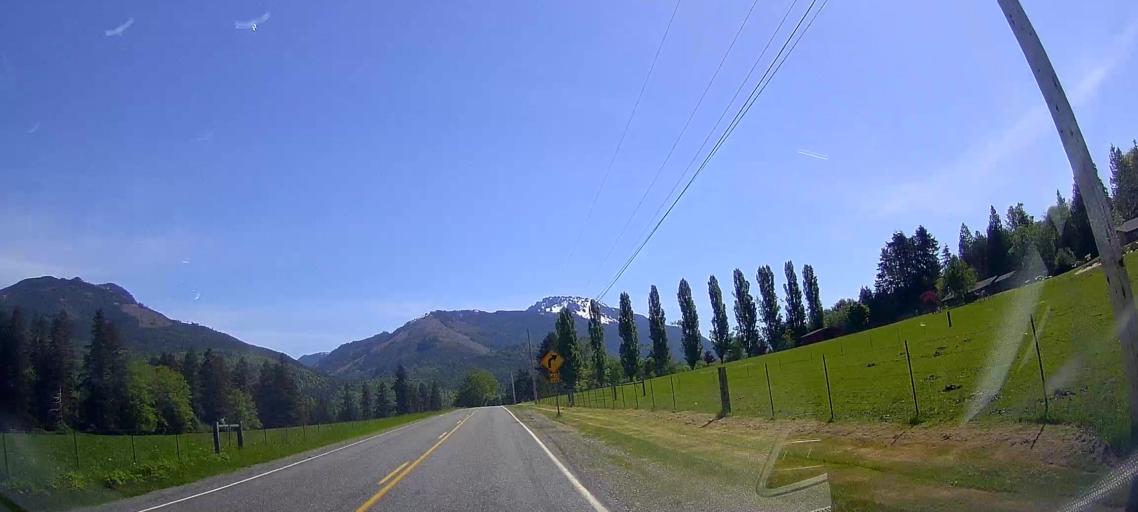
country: US
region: Washington
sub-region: Snohomish County
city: Darrington
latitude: 48.5193
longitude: -121.7327
